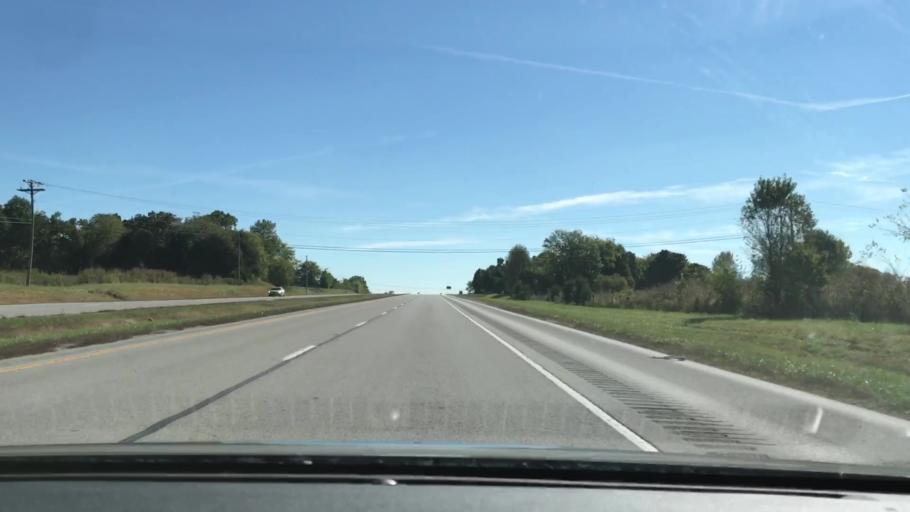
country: US
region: Kentucky
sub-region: Todd County
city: Elkton
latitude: 36.8241
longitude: -87.2072
